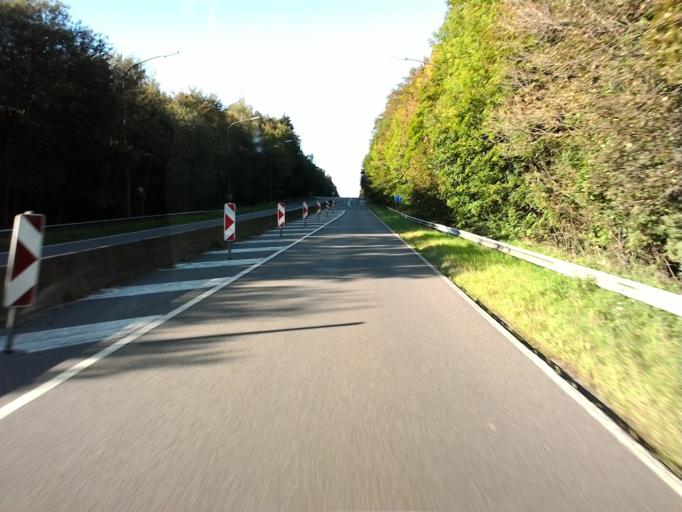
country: BE
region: Wallonia
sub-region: Province du Luxembourg
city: Fauvillers
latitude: 49.8852
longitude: 5.7026
